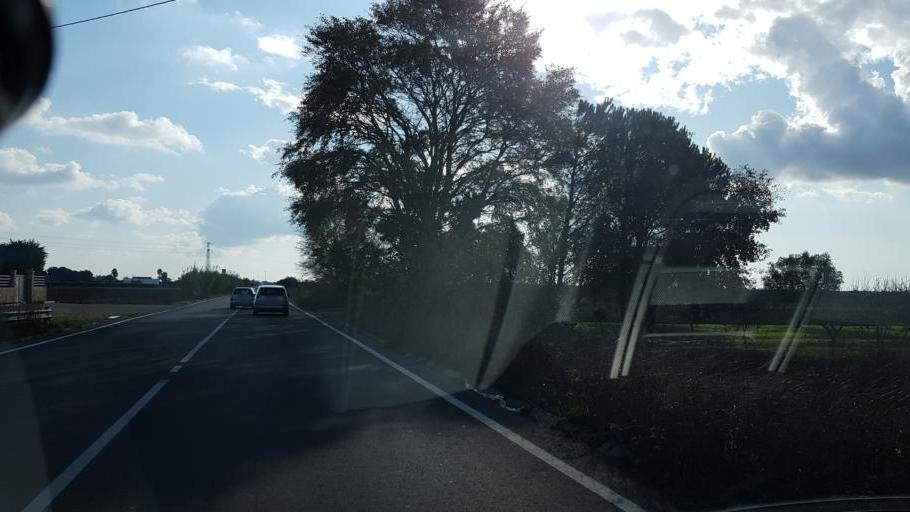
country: IT
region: Apulia
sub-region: Provincia di Lecce
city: Veglie
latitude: 40.3599
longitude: 17.9679
